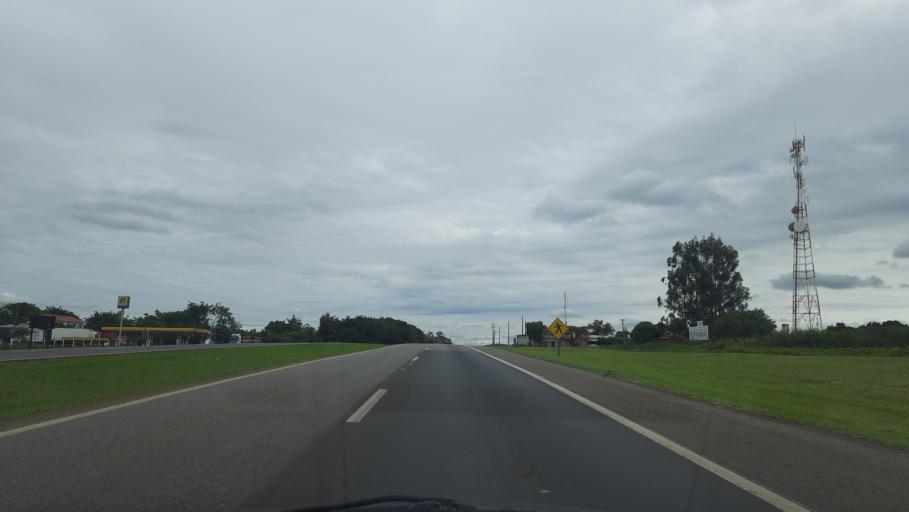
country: BR
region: Sao Paulo
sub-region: Moji-Guacu
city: Mogi-Gaucu
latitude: -22.2216
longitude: -46.9796
